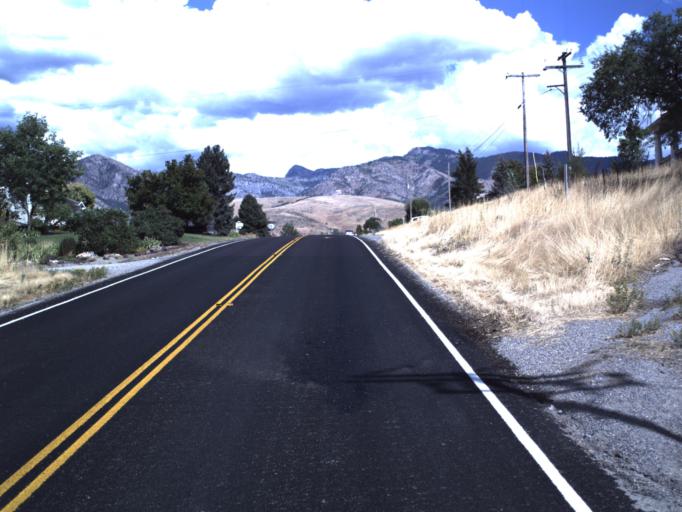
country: US
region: Utah
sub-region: Cache County
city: Richmond
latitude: 41.9229
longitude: -111.8234
